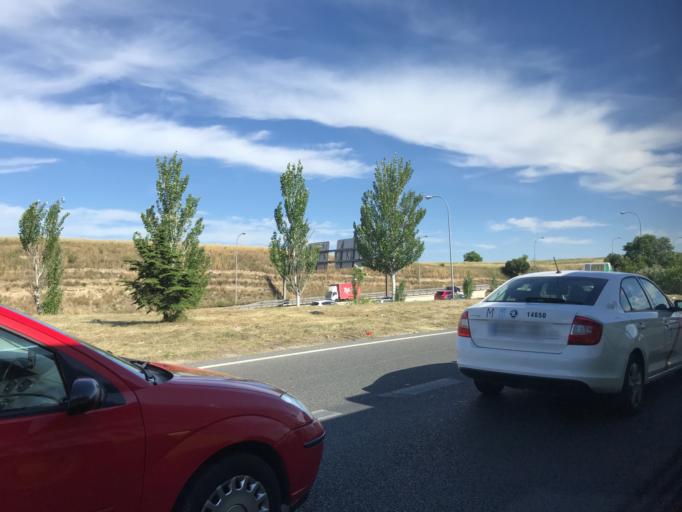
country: ES
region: Madrid
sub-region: Provincia de Madrid
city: San Blas
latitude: 40.4378
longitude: -3.5940
